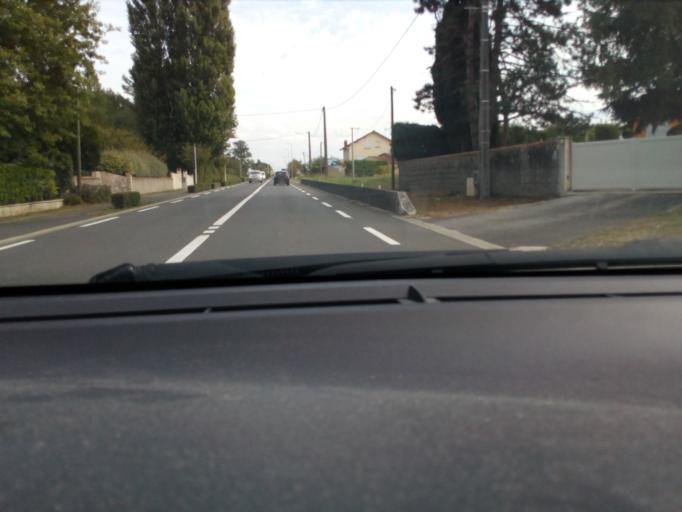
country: FR
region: Poitou-Charentes
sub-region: Departement de la Charente
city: Fleac
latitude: 45.6741
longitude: 0.0938
